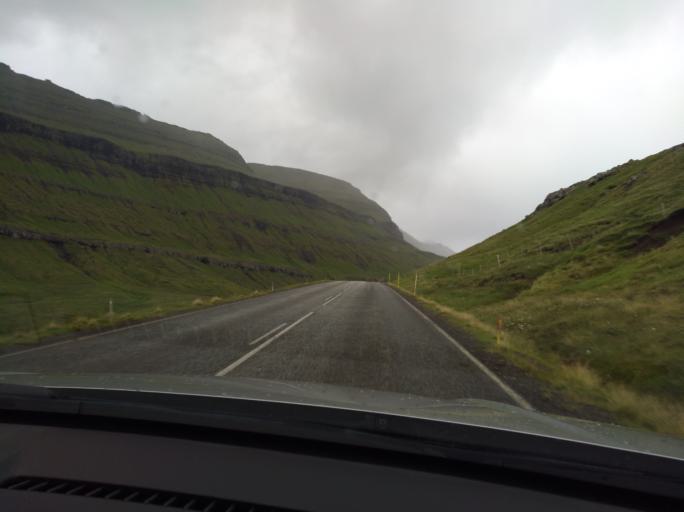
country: FO
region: Eysturoy
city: Fuglafjordur
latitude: 62.2302
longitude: -6.8793
